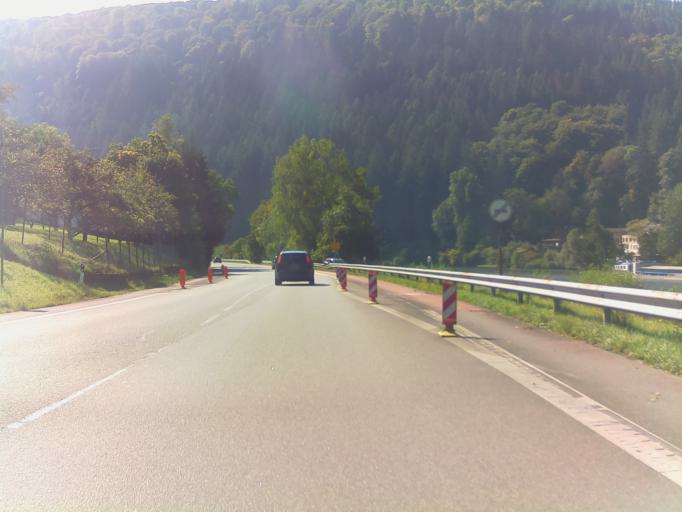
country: DE
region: Baden-Wuerttemberg
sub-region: Karlsruhe Region
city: Neunkirchen
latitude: 49.4220
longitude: 9.0020
